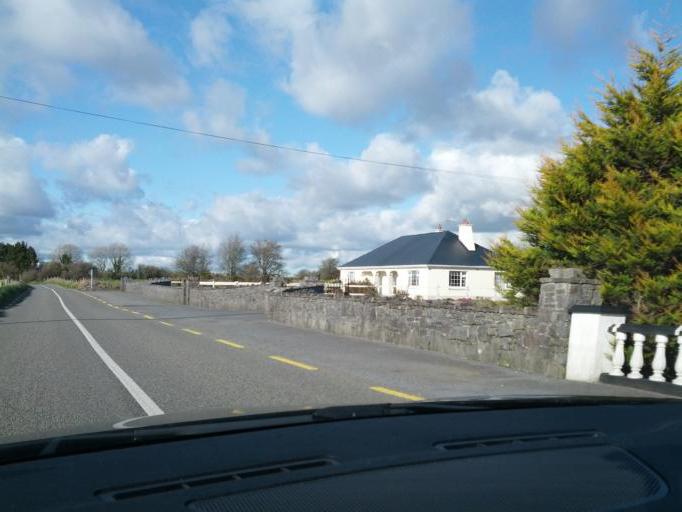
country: IE
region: Connaught
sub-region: Roscommon
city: Castlerea
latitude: 53.5776
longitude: -8.5622
